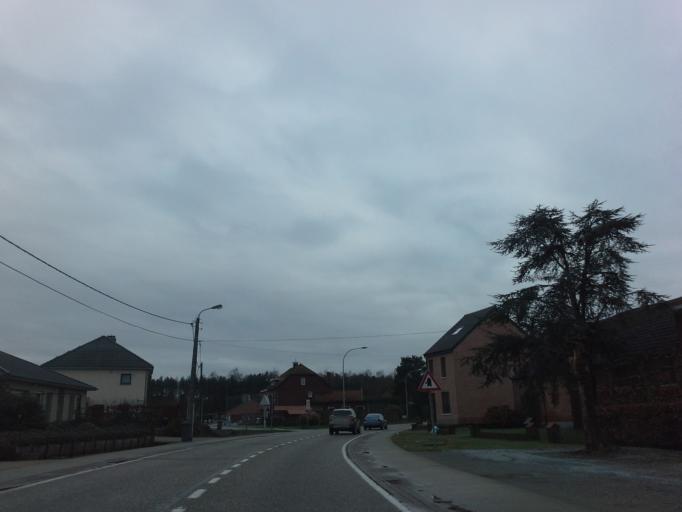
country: BE
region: Flanders
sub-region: Provincie Antwerpen
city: Balen
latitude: 51.1592
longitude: 5.1655
